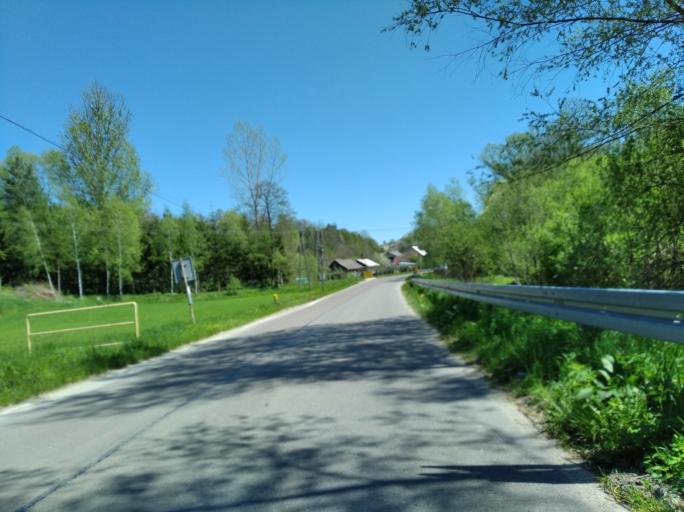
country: PL
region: Subcarpathian Voivodeship
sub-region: Powiat debicki
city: Brzostek
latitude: 49.9151
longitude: 21.3641
